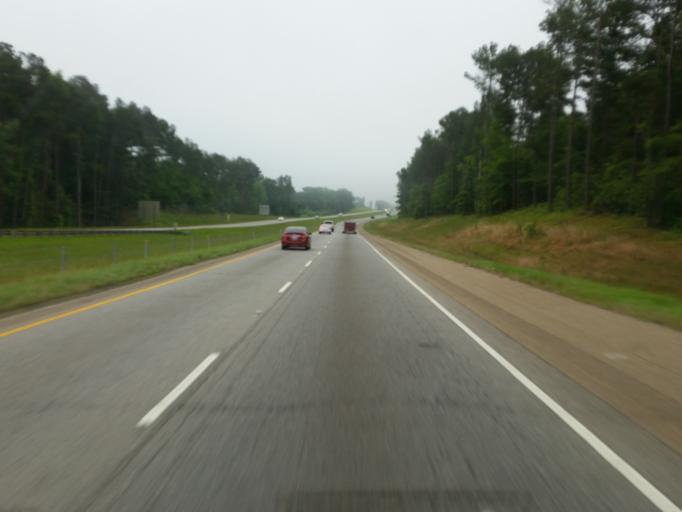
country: US
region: Louisiana
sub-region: Webster Parish
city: Minden
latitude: 32.5878
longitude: -93.2849
